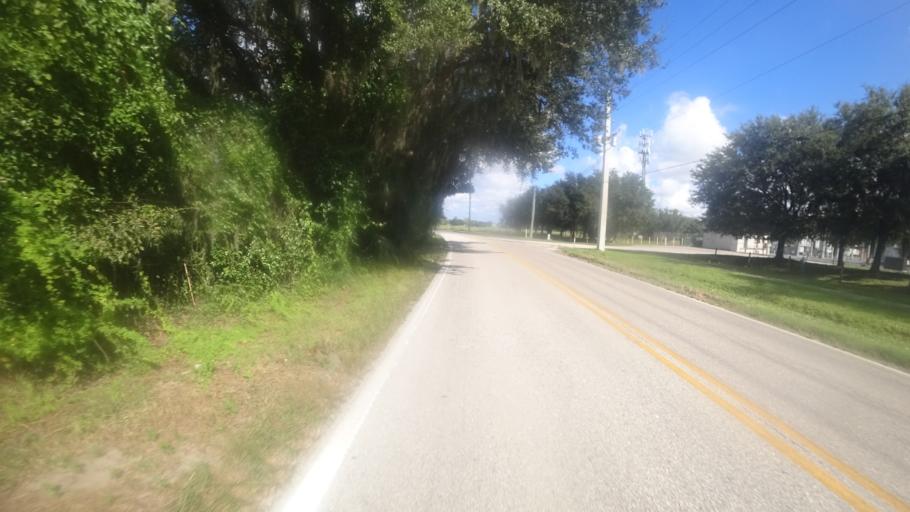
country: US
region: Florida
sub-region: Manatee County
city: Ellenton
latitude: 27.4760
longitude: -82.4566
